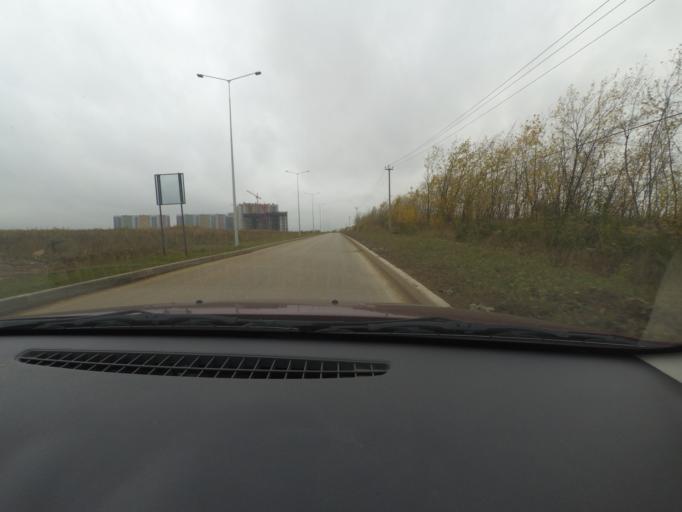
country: RU
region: Nizjnij Novgorod
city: Afonino
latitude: 56.2464
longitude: 44.0569
